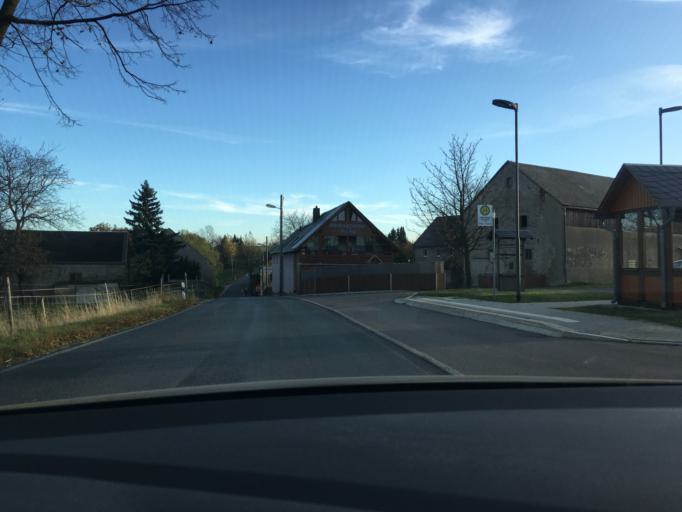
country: DE
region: Saxony
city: Barenstein
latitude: 50.8180
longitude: 13.8117
